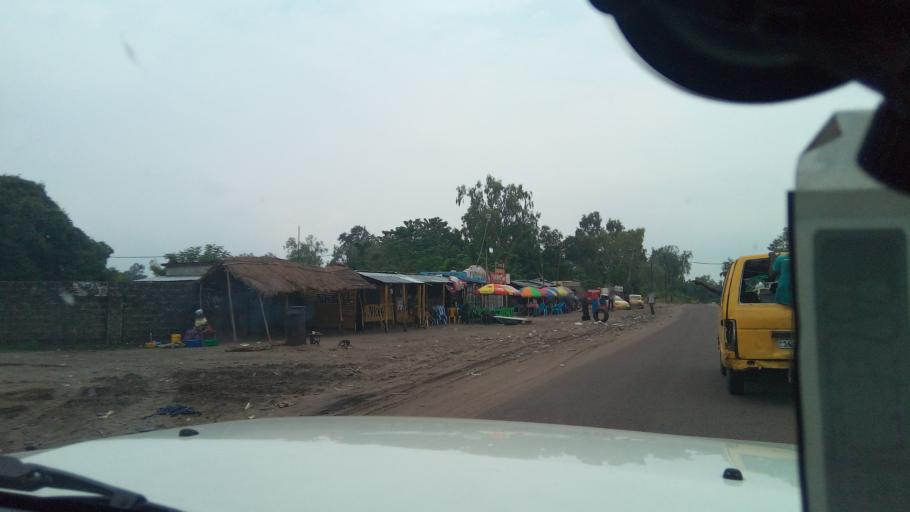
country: CD
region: Kinshasa
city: Masina
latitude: -4.1929
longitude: 15.5542
